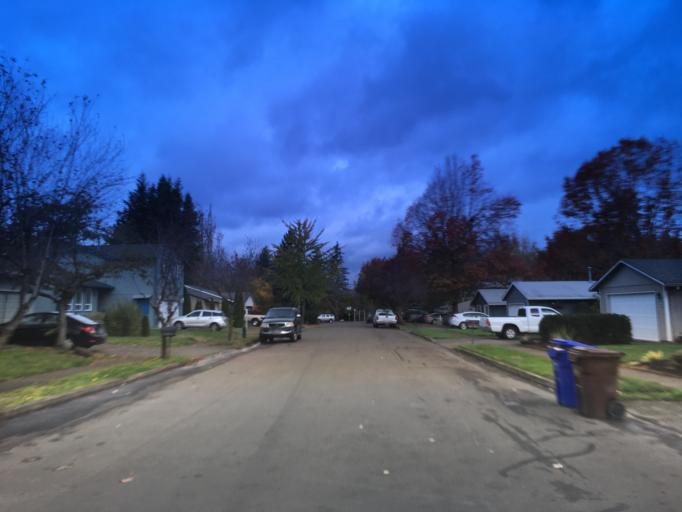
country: US
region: Oregon
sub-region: Multnomah County
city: Fairview
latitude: 45.5370
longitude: -122.4447
